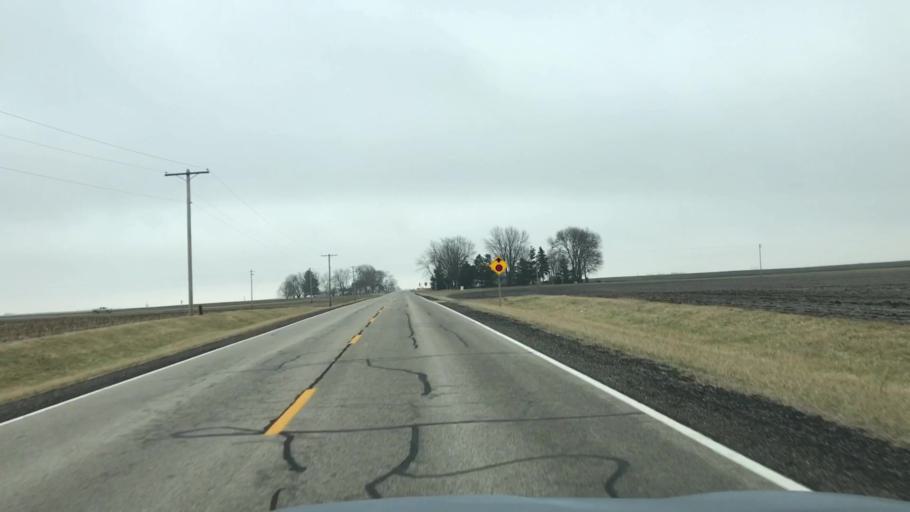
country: US
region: Illinois
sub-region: McLean County
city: Hudson
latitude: 40.6081
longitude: -88.9452
